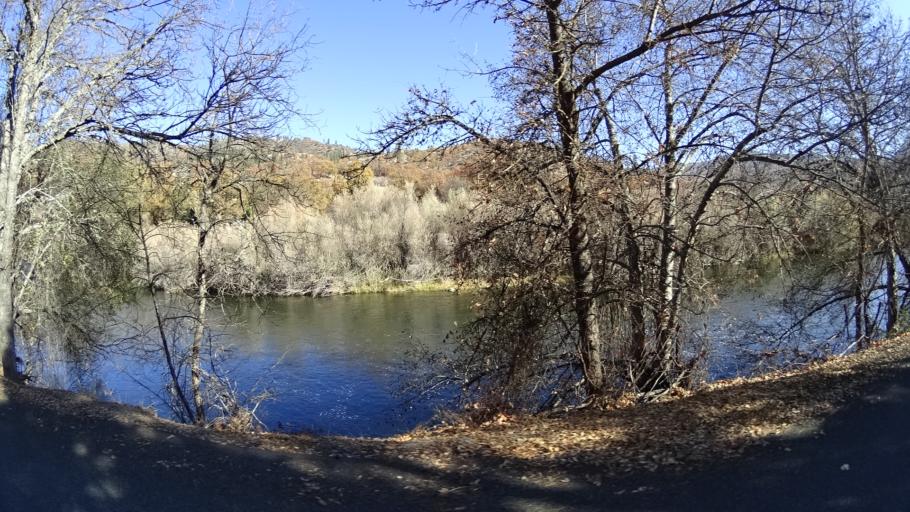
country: US
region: California
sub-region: Siskiyou County
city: Yreka
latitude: 41.8334
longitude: -122.8526
